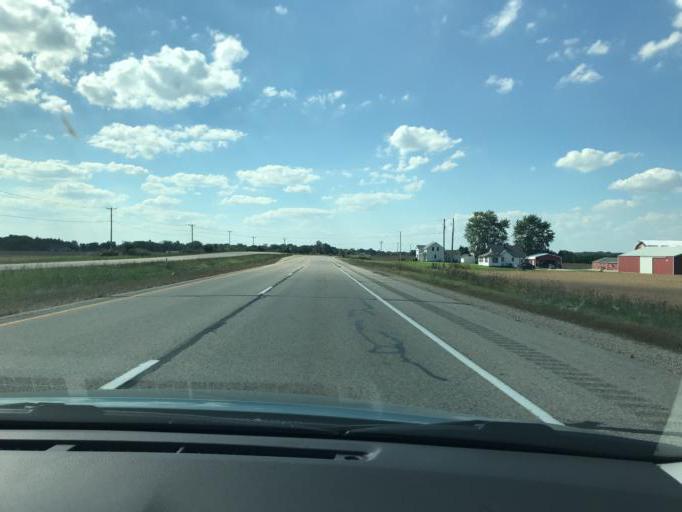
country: US
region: Wisconsin
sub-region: Kenosha County
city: Powers Lake
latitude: 42.5817
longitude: -88.3236
